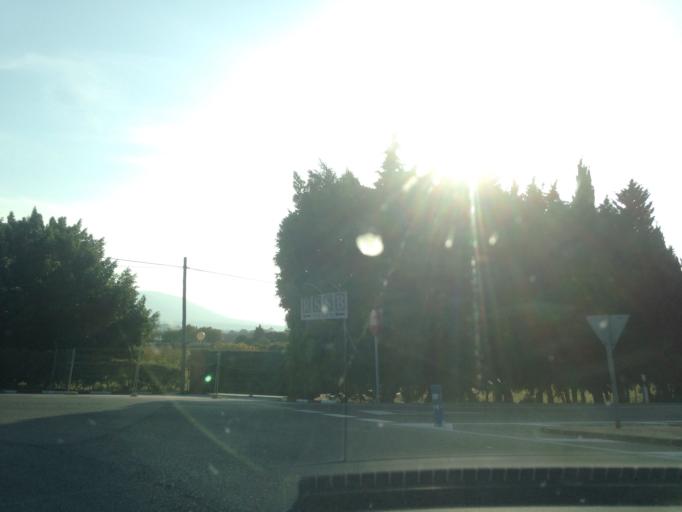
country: ES
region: Andalusia
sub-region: Provincia de Malaga
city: Alhaurin de la Torre
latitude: 36.6828
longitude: -4.5374
